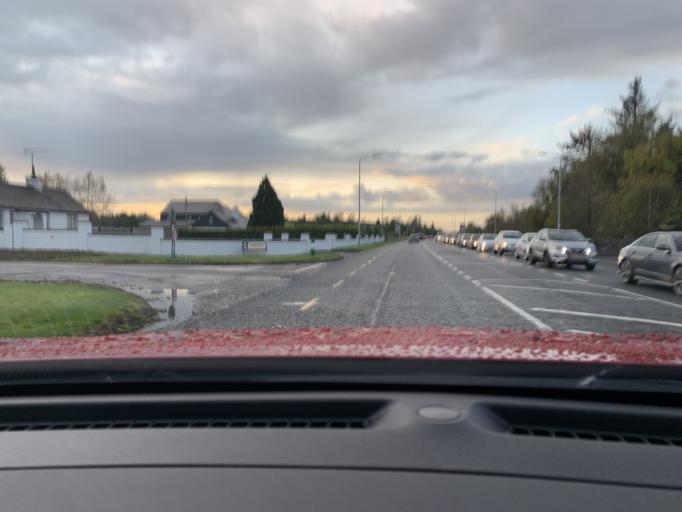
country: IE
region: Connaught
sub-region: County Leitrim
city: Carrick-on-Shannon
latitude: 53.9441
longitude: -8.1145
